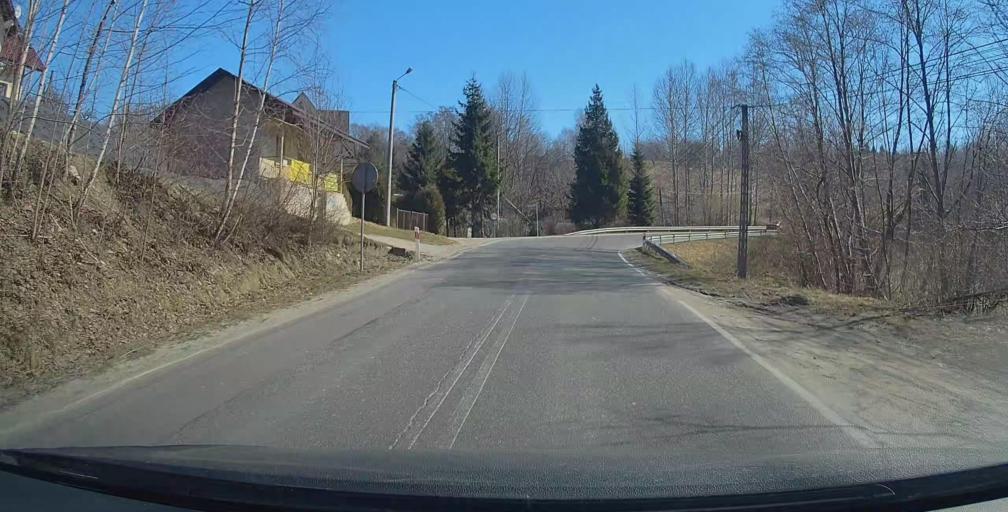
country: PL
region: Subcarpathian Voivodeship
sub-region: Powiat rzeszowski
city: Hyzne
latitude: 49.8995
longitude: 22.2182
